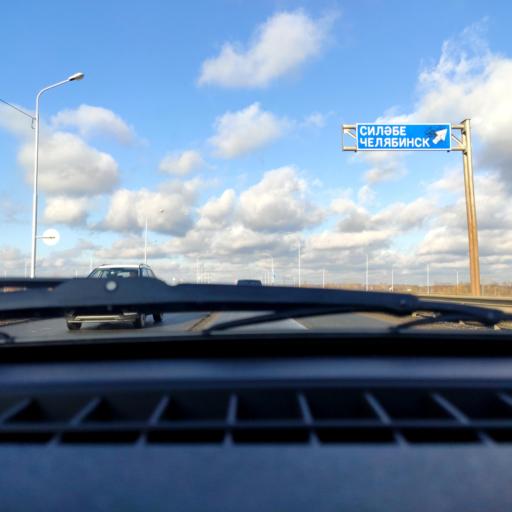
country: RU
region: Bashkortostan
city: Kabakovo
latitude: 54.6473
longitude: 56.0836
